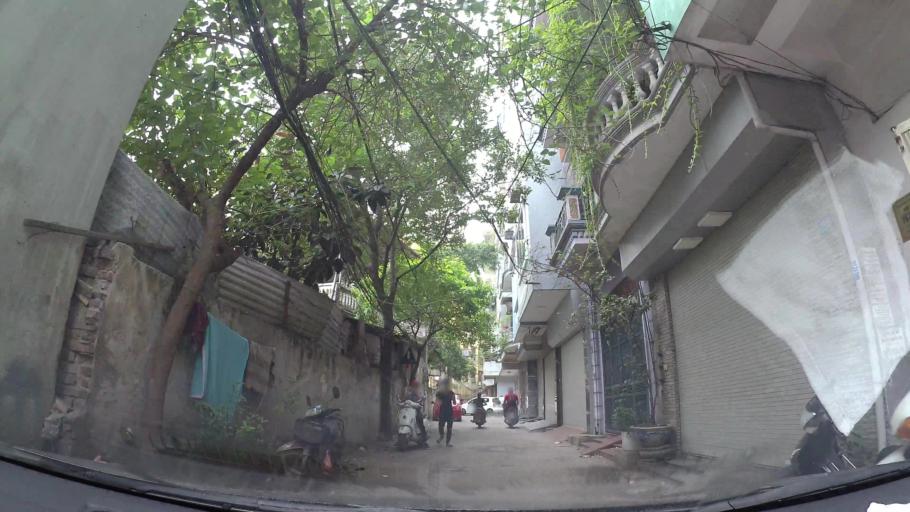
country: VN
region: Ha Noi
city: Hai BaTrung
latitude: 20.9875
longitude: 105.8660
